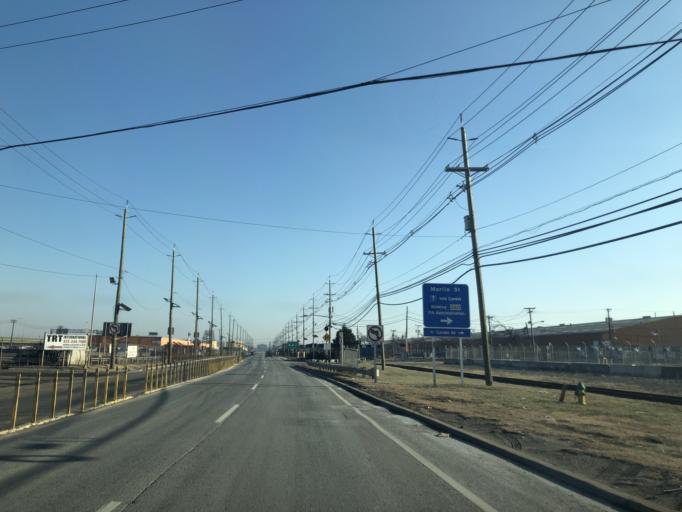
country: US
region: New Jersey
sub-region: Essex County
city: Newark
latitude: 40.7027
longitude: -74.1458
